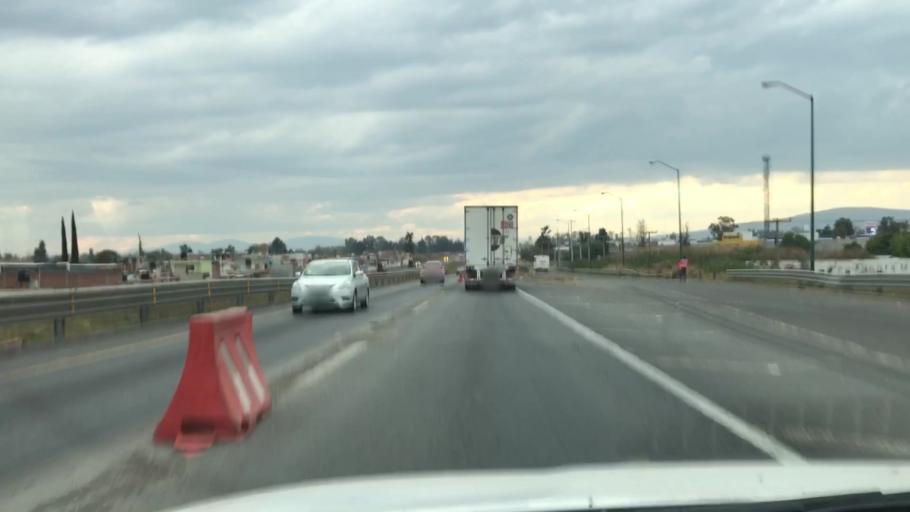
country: MX
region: Guanajuato
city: Irapuato
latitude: 20.6501
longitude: -101.3427
